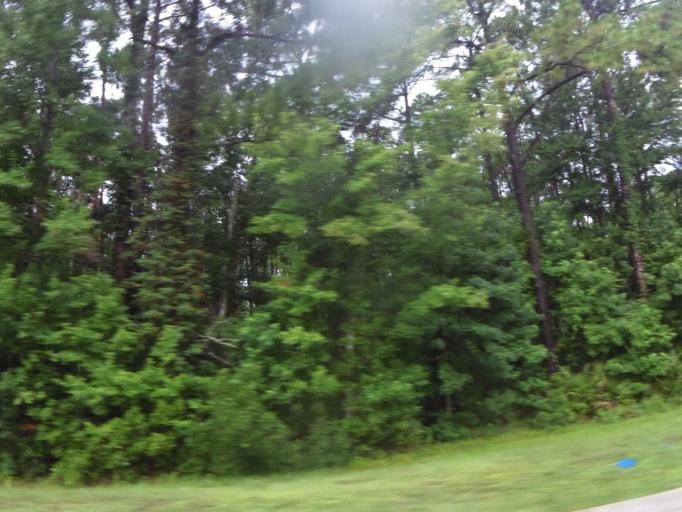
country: US
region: Florida
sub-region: Duval County
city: Jacksonville Beach
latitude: 30.2708
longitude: -81.5110
